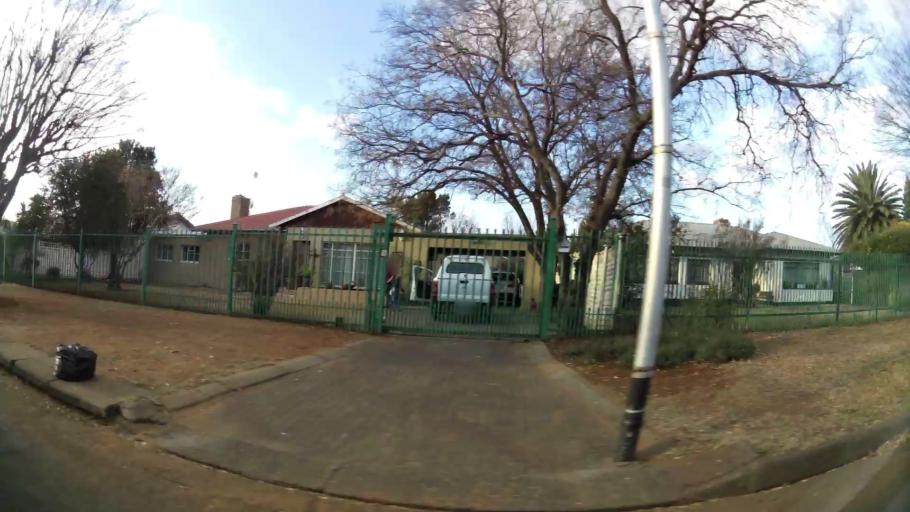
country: ZA
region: Orange Free State
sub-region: Mangaung Metropolitan Municipality
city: Bloemfontein
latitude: -29.1398
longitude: 26.1976
